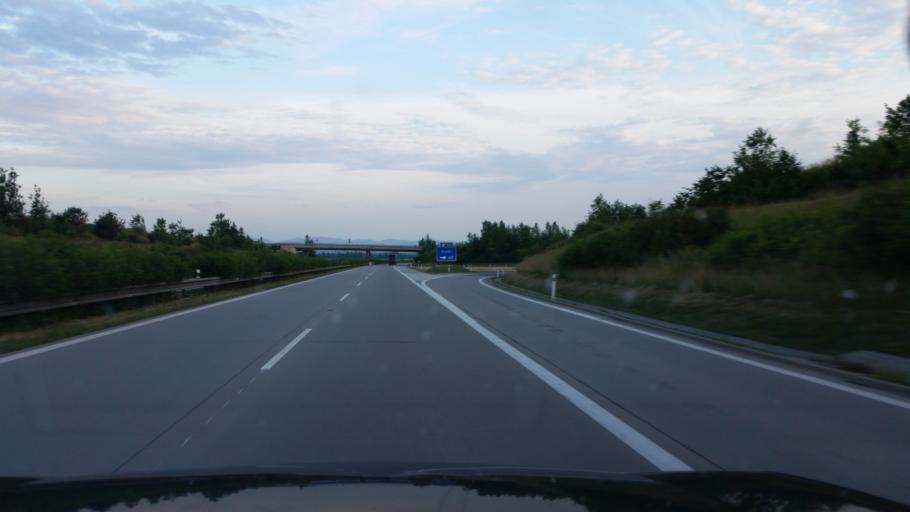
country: CZ
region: Moravskoslezsky
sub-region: Okres Novy Jicin
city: Jistebnik
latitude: 49.7577
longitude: 18.0958
